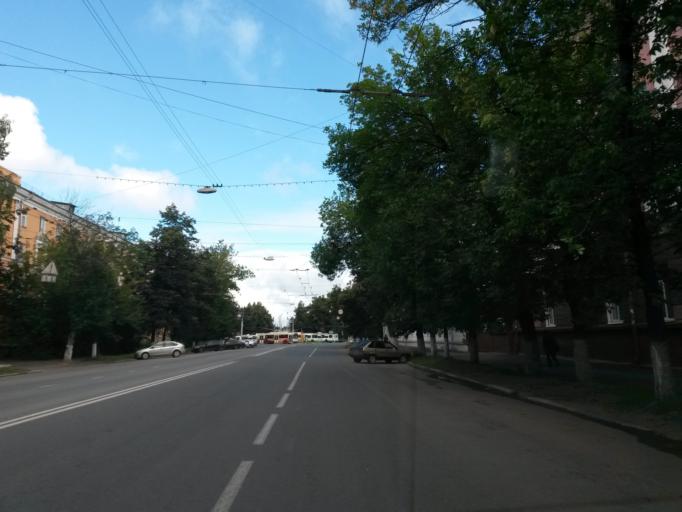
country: RU
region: Jaroslavl
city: Yaroslavl
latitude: 57.6411
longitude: 39.8750
